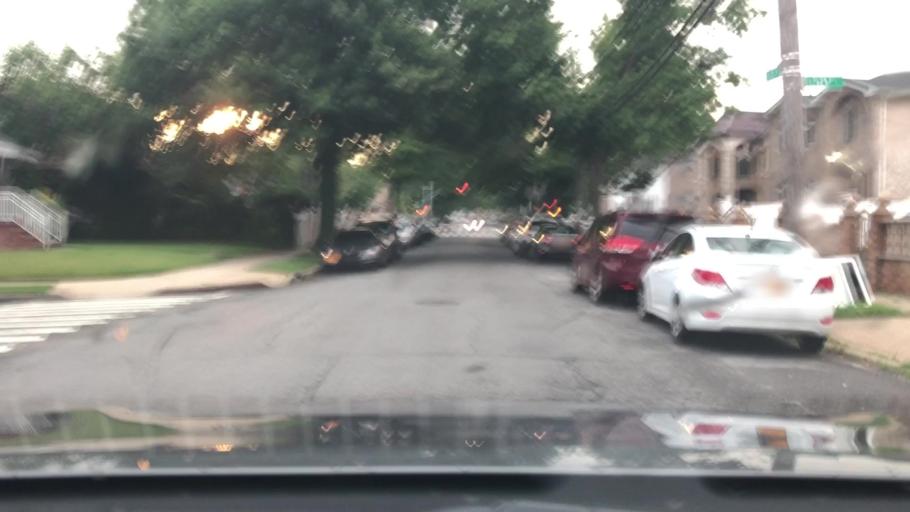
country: US
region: New York
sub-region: Queens County
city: Jamaica
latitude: 40.6697
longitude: -73.8084
